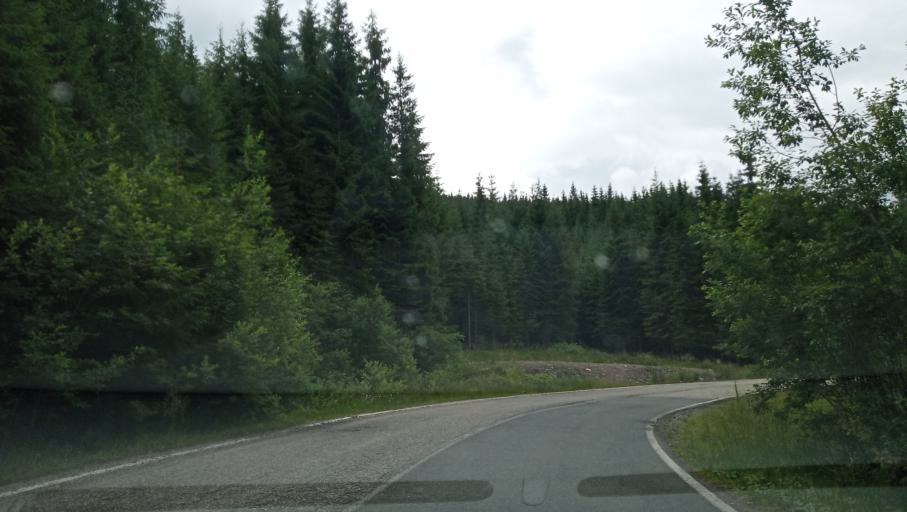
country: RO
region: Valcea
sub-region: Comuna Voineasa
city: Voineasa
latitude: 45.4240
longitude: 23.7674
